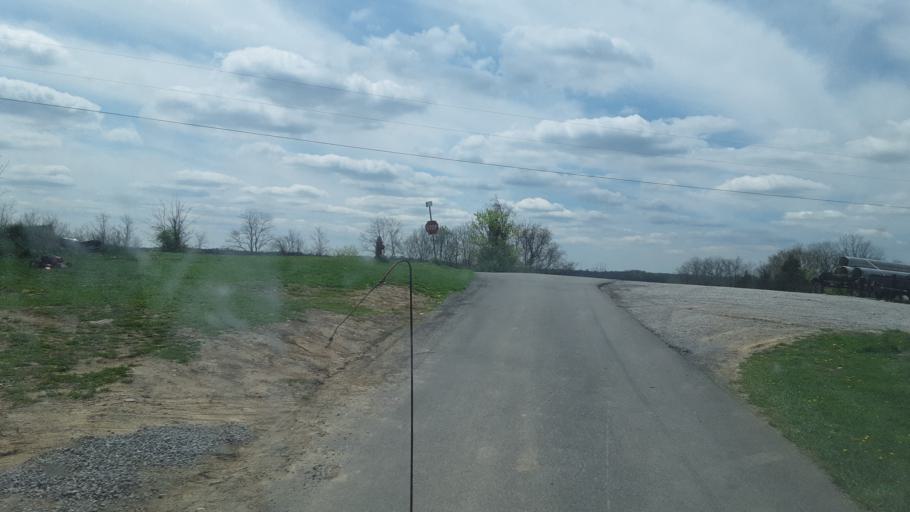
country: US
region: Kentucky
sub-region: Owen County
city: Owenton
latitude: 38.6735
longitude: -84.7840
